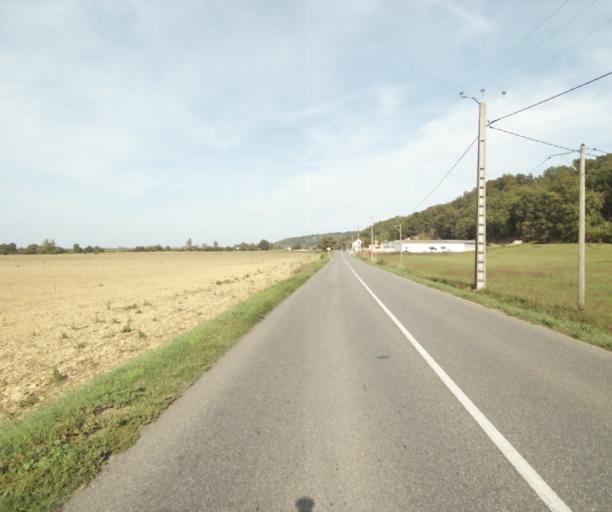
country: FR
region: Midi-Pyrenees
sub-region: Departement du Tarn-et-Garonne
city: Corbarieu
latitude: 43.9498
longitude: 1.3646
